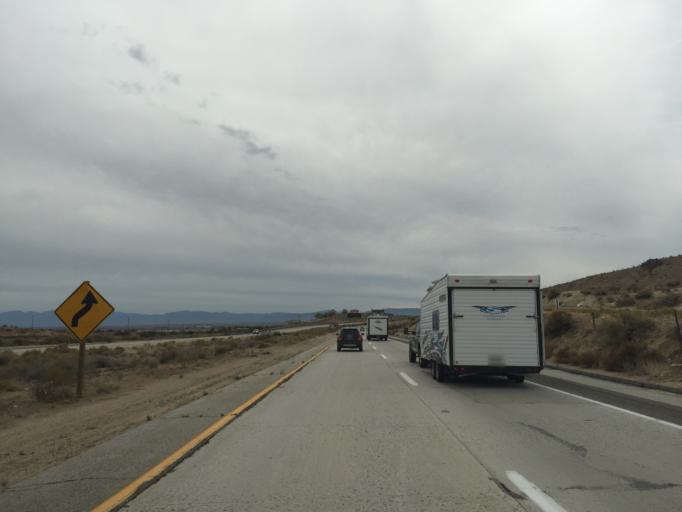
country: US
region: California
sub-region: Kern County
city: Rosamond
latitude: 34.8829
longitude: -118.1665
